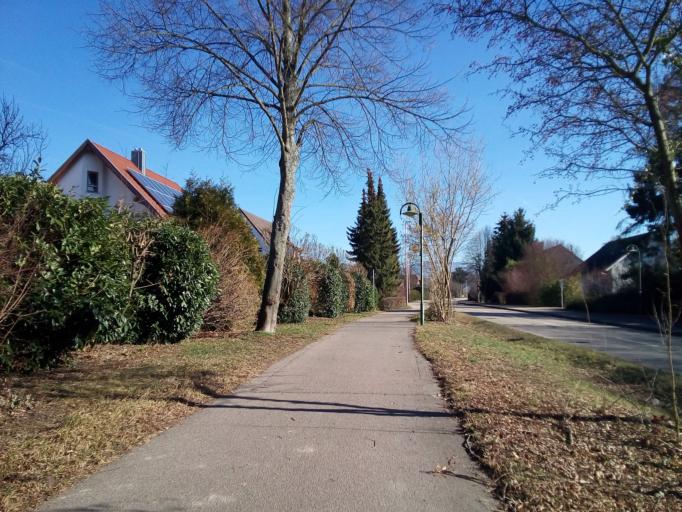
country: DE
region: Baden-Wuerttemberg
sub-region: Freiburg Region
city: Renchen
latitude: 48.6083
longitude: 8.0290
